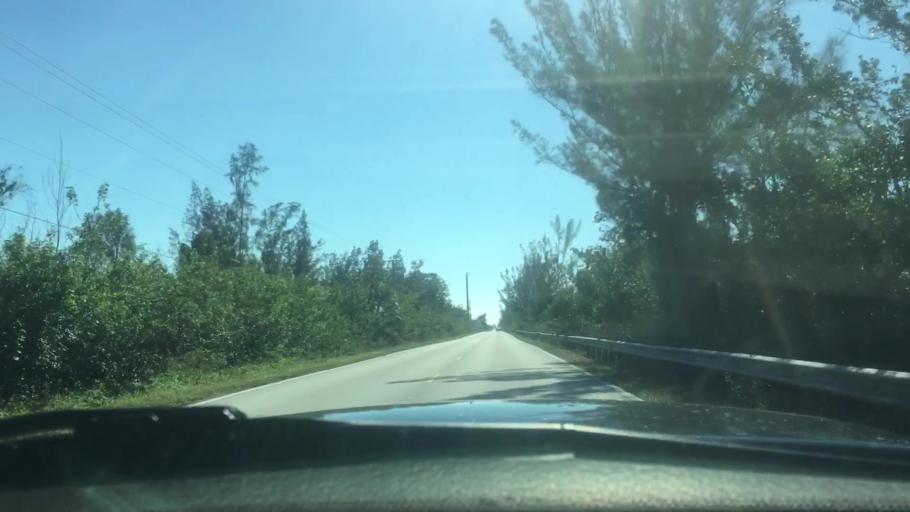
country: US
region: Florida
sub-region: Miami-Dade County
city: Florida City
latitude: 25.3659
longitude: -80.4292
